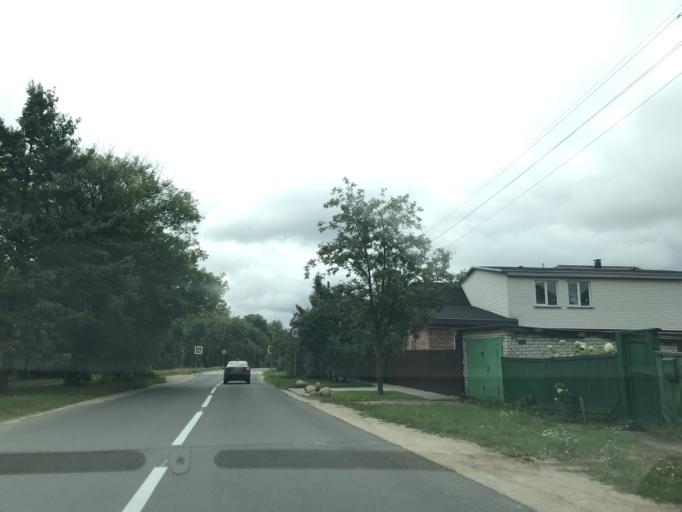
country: BY
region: Minsk
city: Minsk
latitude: 53.9377
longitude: 27.6235
